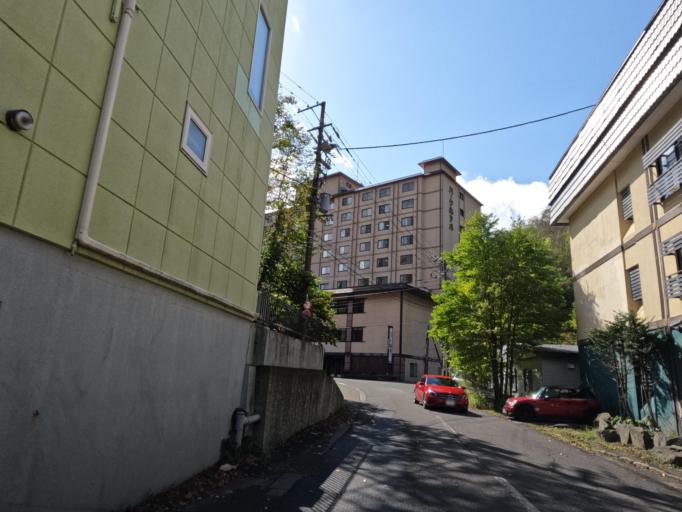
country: JP
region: Hokkaido
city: Shiraoi
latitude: 42.4964
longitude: 141.1414
